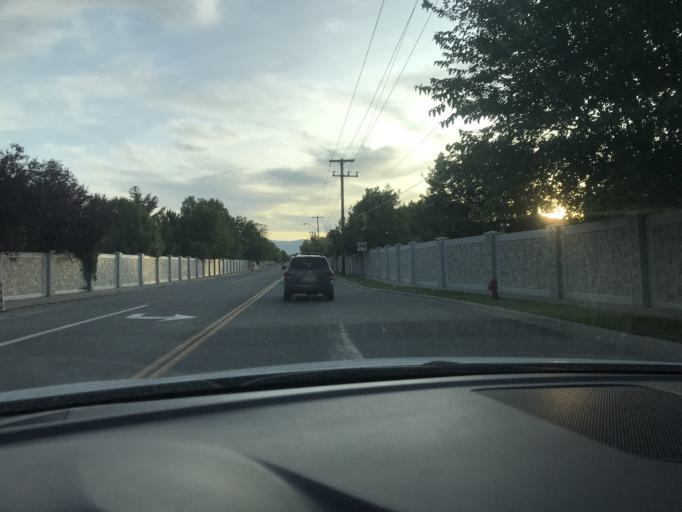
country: US
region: Utah
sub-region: Salt Lake County
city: South Jordan Heights
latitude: 40.5732
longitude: -111.9485
